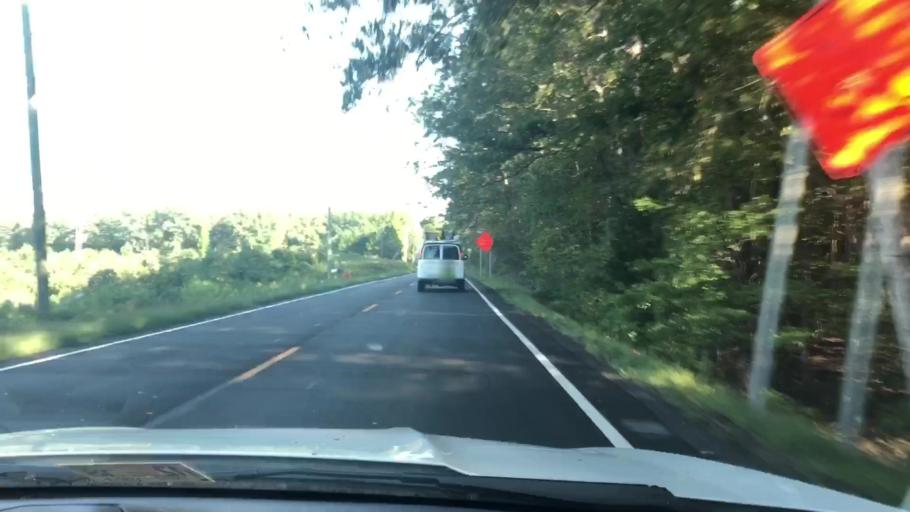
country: US
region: Virginia
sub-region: King William County
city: West Point
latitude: 37.4651
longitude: -76.8430
